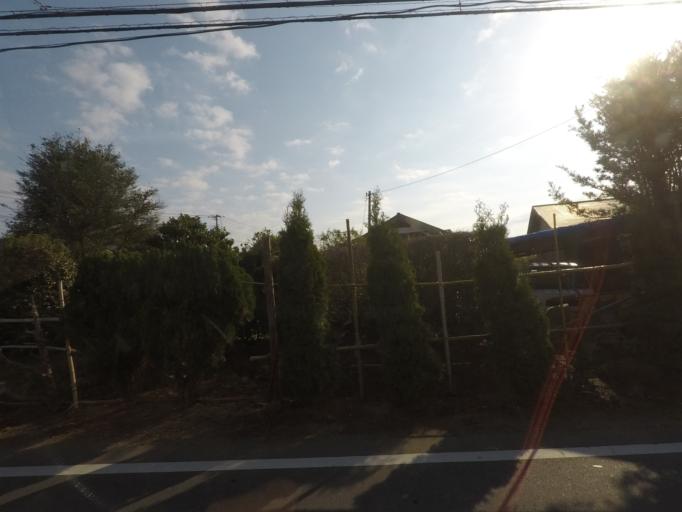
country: JP
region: Chiba
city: Yachimata
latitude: 35.6501
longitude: 140.2909
